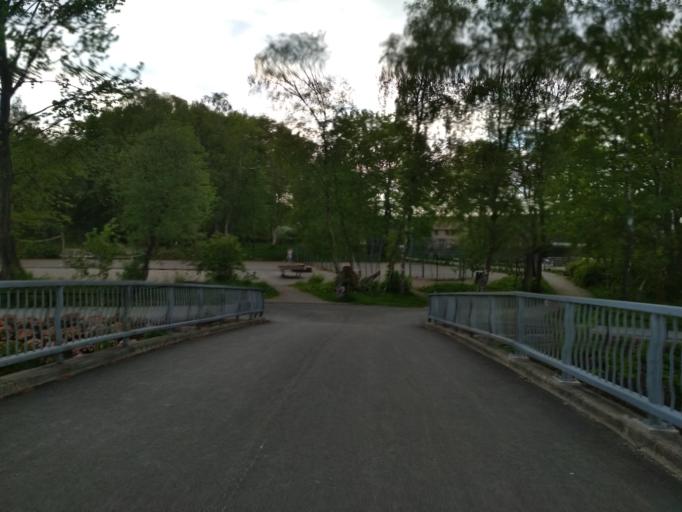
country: NO
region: Rogaland
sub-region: Stavanger
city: Stavanger
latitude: 58.9590
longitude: 5.7223
